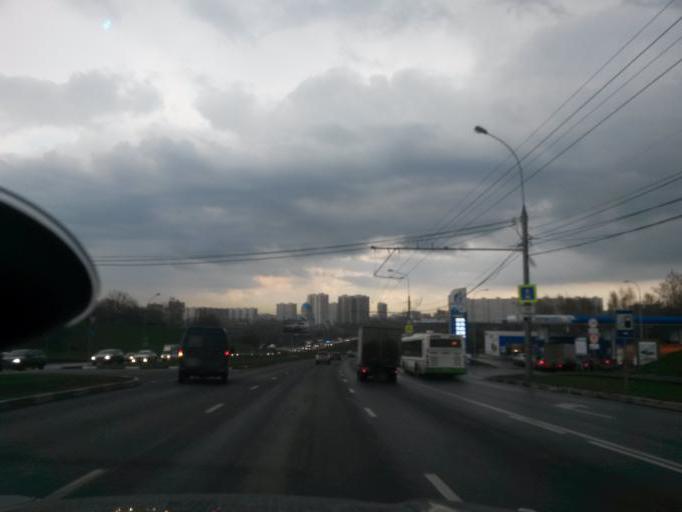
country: RU
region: Moskovskaya
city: Kur'yanovo
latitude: 55.6337
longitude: 37.7012
